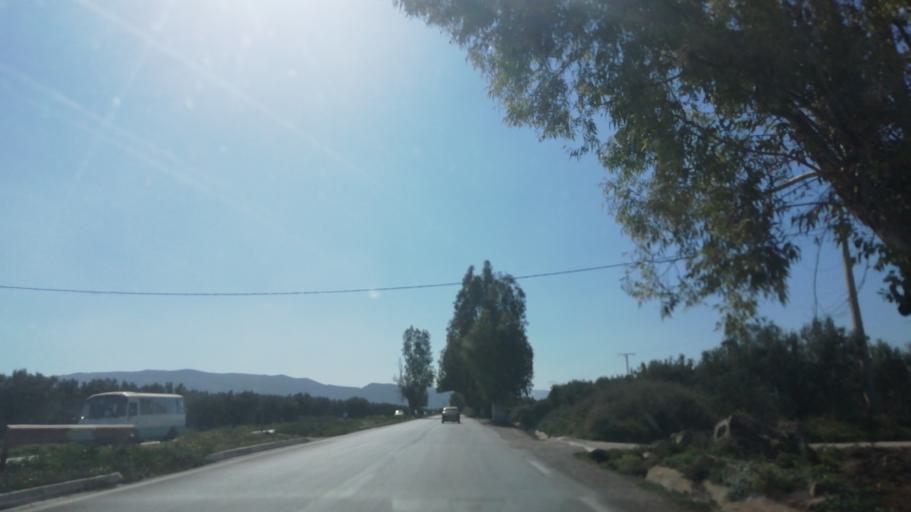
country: DZ
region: Mascara
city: Sig
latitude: 35.5521
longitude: -0.2065
